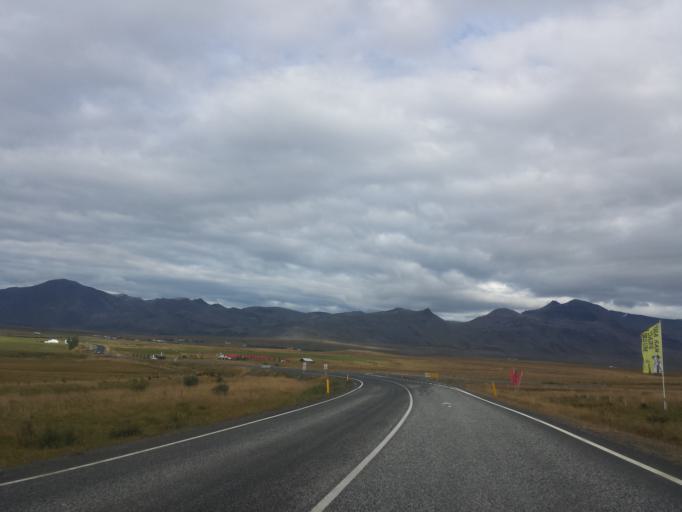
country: IS
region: West
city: Borgarnes
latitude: 64.3850
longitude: -21.8470
